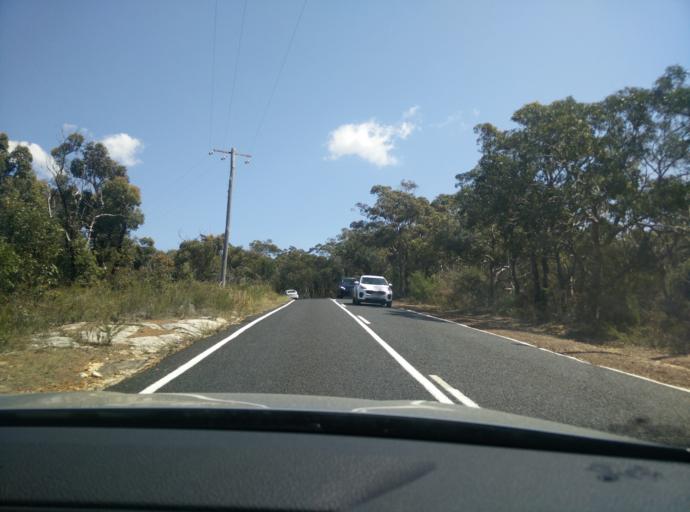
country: AU
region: New South Wales
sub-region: Gosford Shire
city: Umina
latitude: -33.5366
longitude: 151.2867
